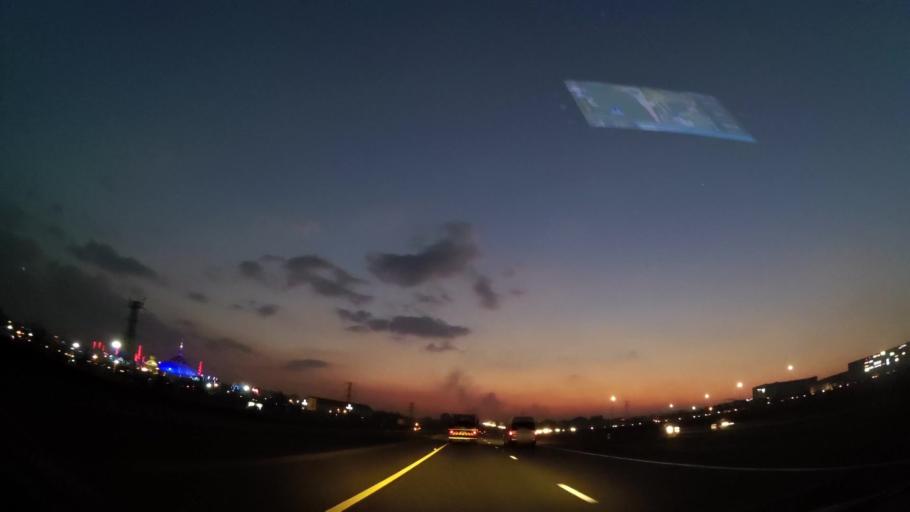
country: ZA
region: Gauteng
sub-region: Ekurhuleni Metropolitan Municipality
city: Brakpan
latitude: -26.2553
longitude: 28.3203
